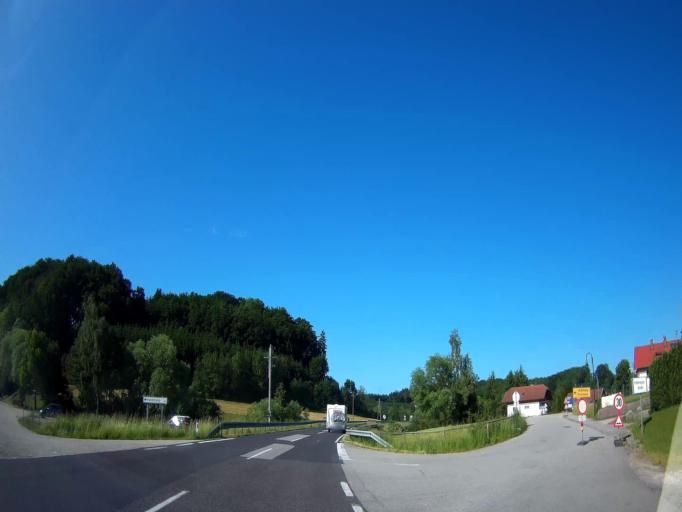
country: AT
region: Salzburg
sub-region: Politischer Bezirk Salzburg-Umgebung
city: Dorfbeuern
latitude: 48.1255
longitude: 13.0082
